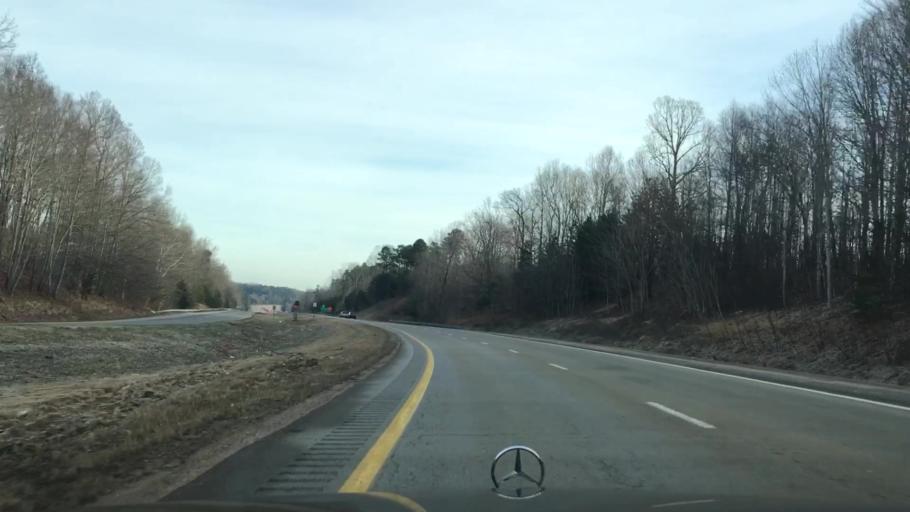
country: US
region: Virginia
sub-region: City of Danville
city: Danville
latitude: 36.5493
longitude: -79.3932
